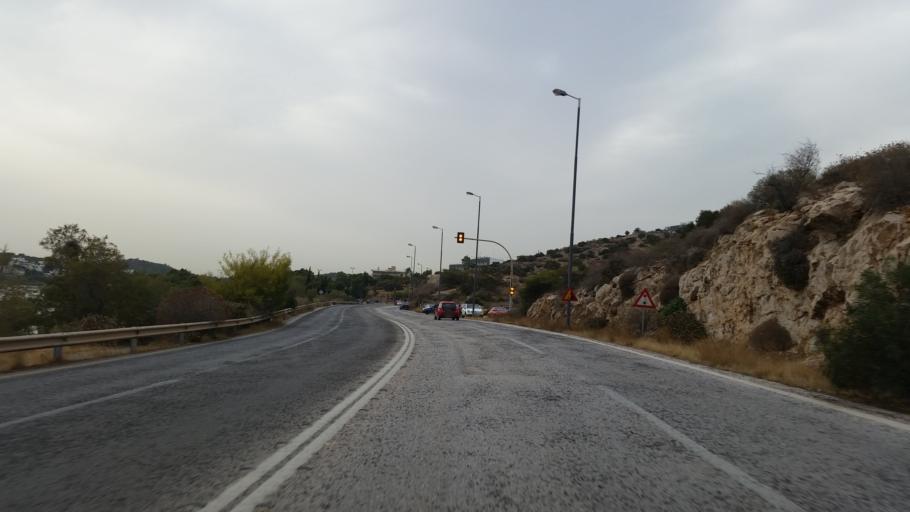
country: GR
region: Attica
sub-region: Nomarchia Anatolikis Attikis
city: Vouliagmeni
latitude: 37.8054
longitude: 23.7849
